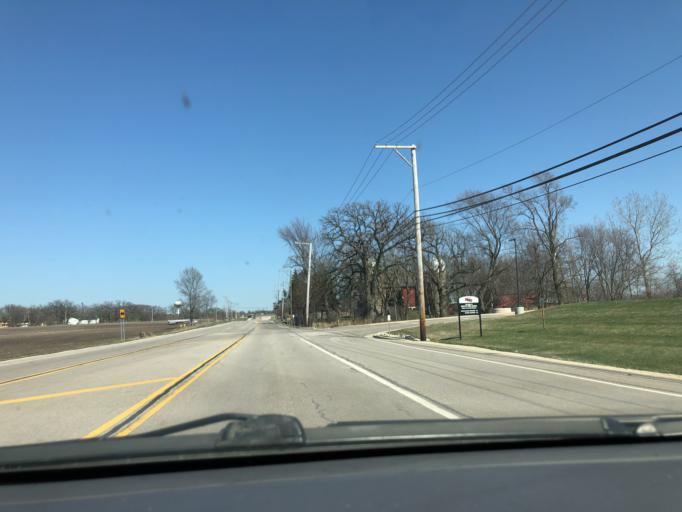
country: US
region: Illinois
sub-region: McHenry County
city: Huntley
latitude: 42.1657
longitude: -88.4627
